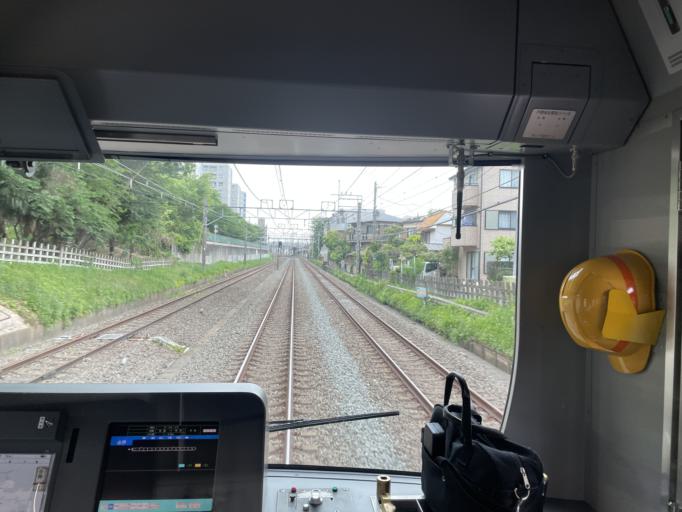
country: JP
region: Saitama
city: Tokorozawa
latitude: 35.7870
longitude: 139.4842
